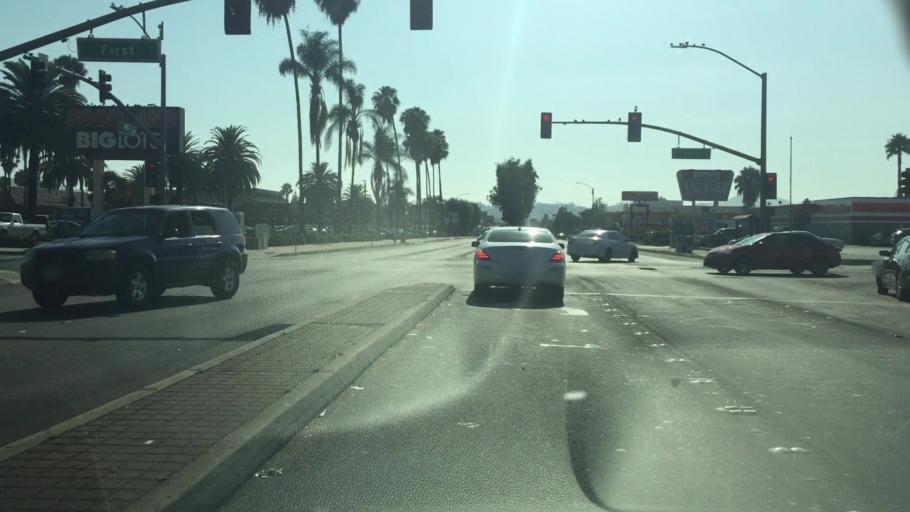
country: US
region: California
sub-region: San Diego County
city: Bostonia
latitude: 32.7950
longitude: -116.9443
